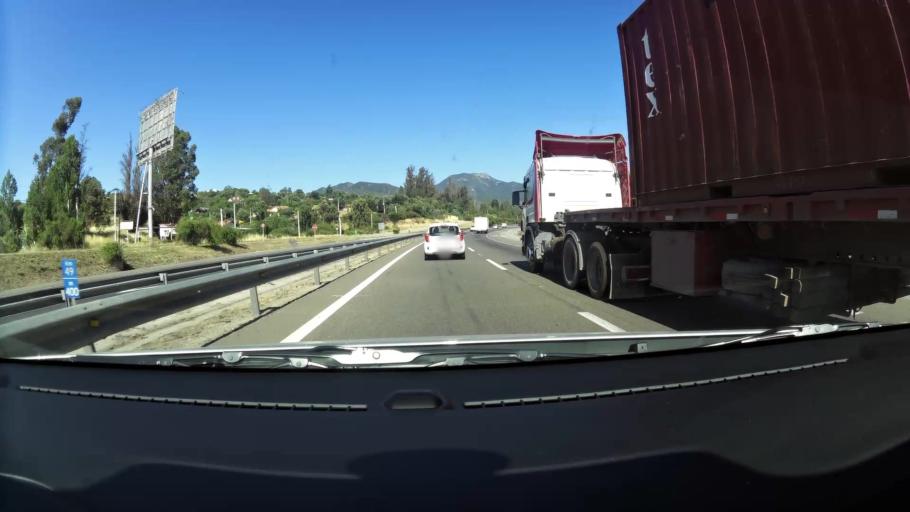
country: CL
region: Santiago Metropolitan
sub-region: Provincia de Melipilla
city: Melipilla
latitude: -33.4055
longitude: -71.2042
